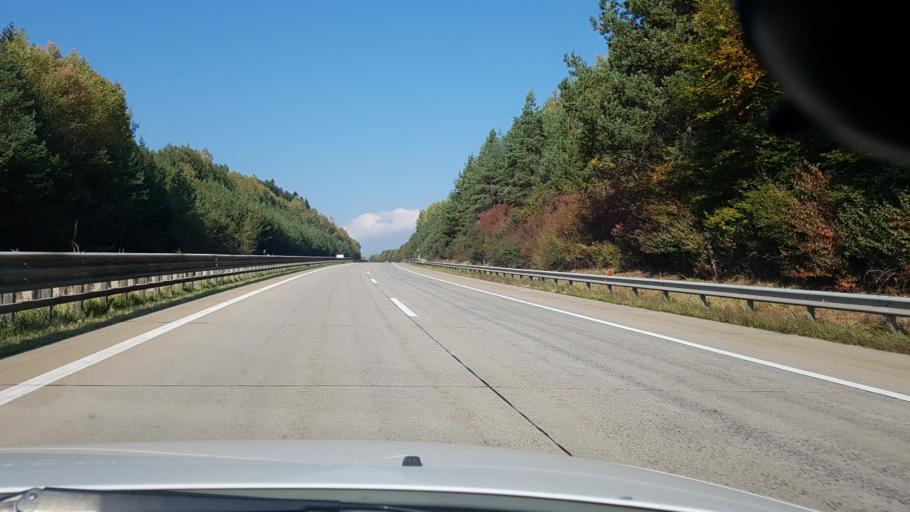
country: AT
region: Carinthia
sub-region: Politischer Bezirk Villach Land
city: Paternion
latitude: 46.7038
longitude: 13.6373
